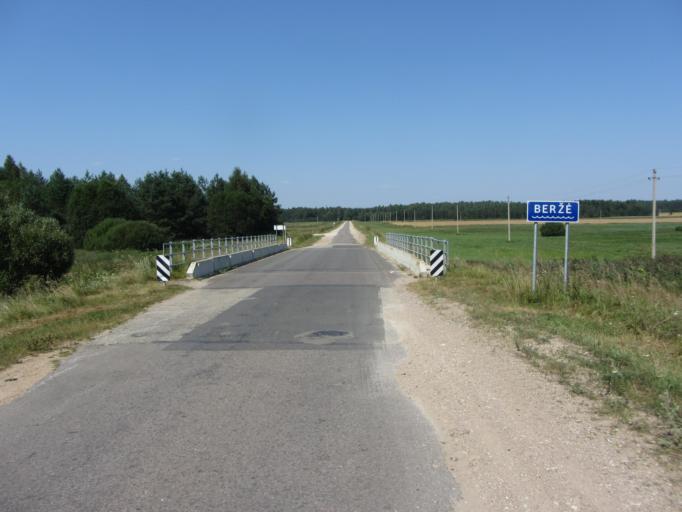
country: LT
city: Salcininkai
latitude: 54.2971
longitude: 25.2112
